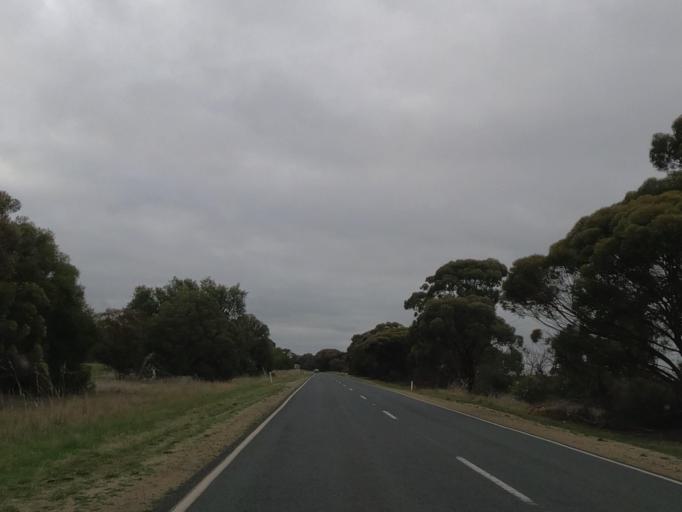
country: AU
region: Victoria
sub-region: Greater Bendigo
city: Long Gully
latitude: -36.3676
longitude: 143.9758
